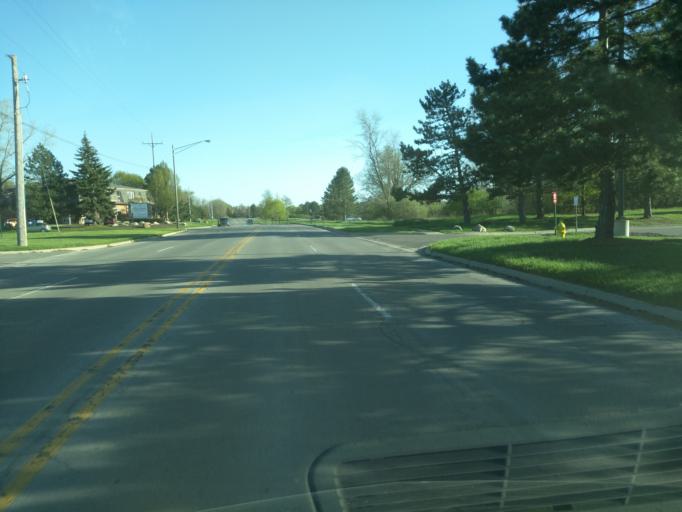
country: US
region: Michigan
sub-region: Eaton County
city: Waverly
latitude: 42.7381
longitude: -84.6326
